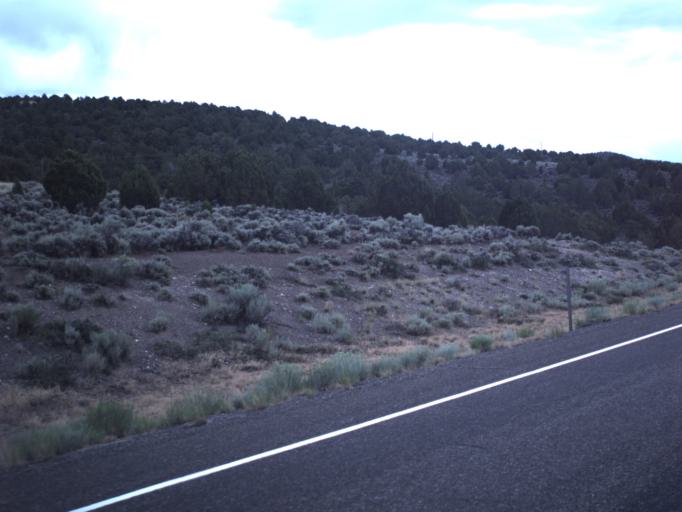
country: US
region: Utah
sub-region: Wayne County
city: Loa
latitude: 38.5388
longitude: -111.8361
